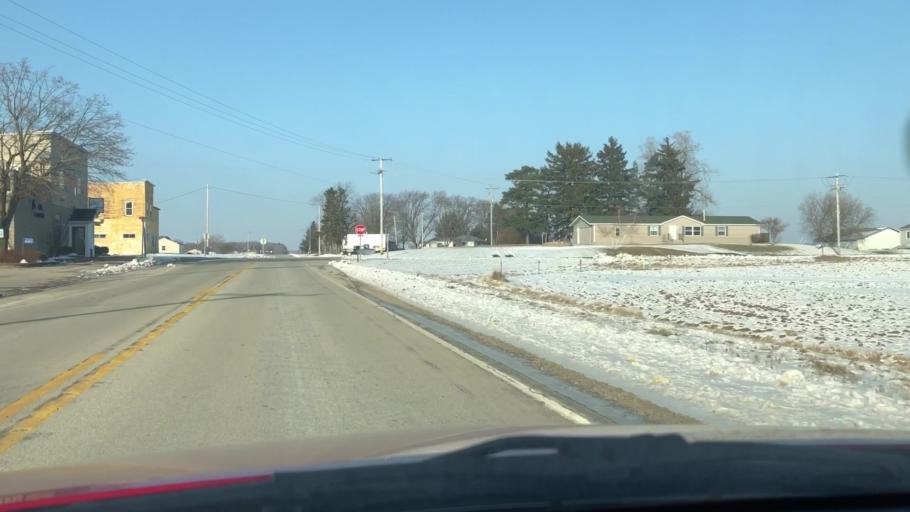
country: US
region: Wisconsin
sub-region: Outagamie County
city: Black Creek
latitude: 44.4140
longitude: -88.3743
